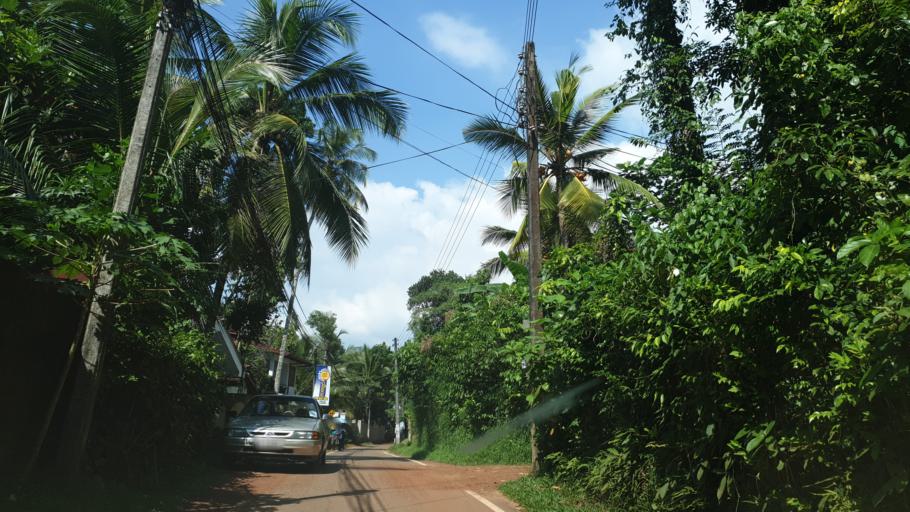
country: LK
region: Western
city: Panadura
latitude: 6.7109
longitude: 79.9599
